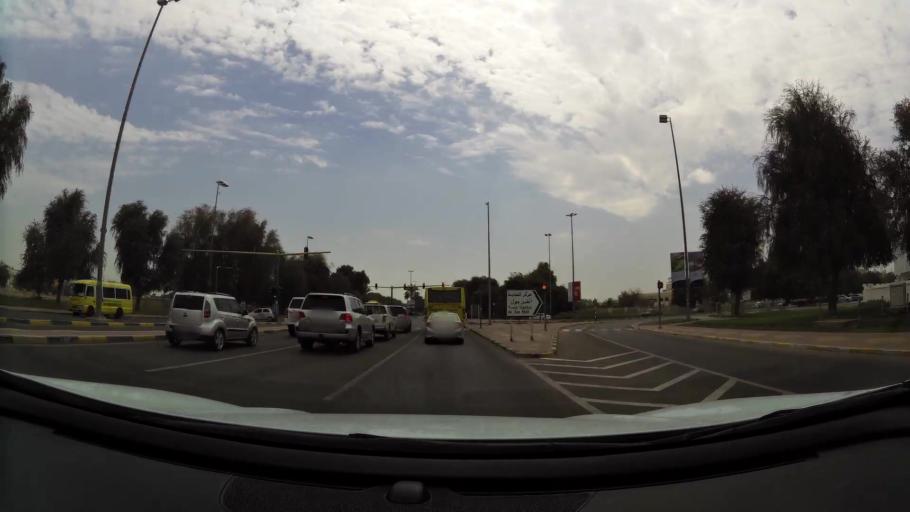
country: OM
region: Al Buraimi
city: Al Buraymi
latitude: 24.2252
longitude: 55.7846
